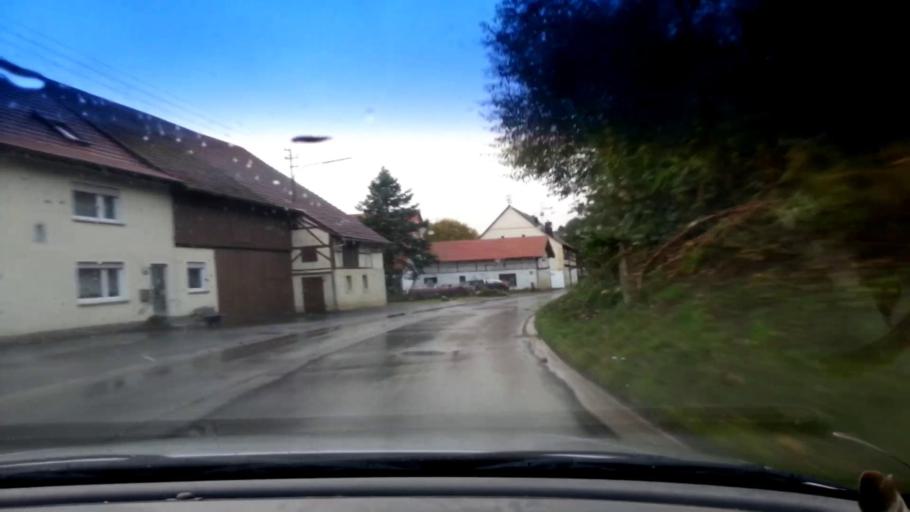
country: DE
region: Bavaria
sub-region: Upper Franconia
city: Schesslitz
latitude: 50.0095
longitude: 11.0732
